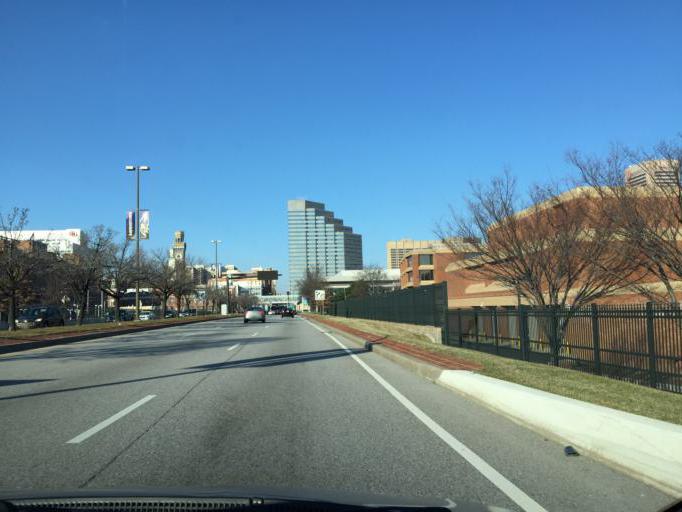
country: US
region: Maryland
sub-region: City of Baltimore
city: Baltimore
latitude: 39.2816
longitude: -76.6189
